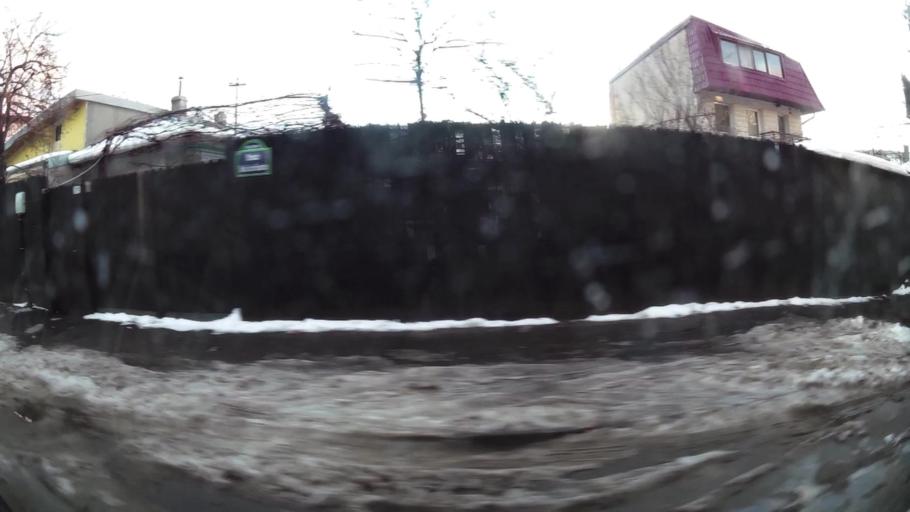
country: RO
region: Ilfov
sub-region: Comuna Popesti-Leordeni
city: Popesti-Leordeni
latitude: 44.3801
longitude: 26.1373
